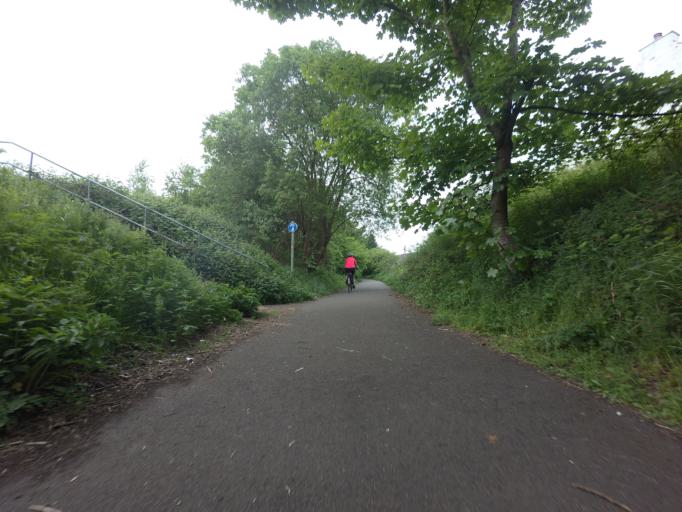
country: GB
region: Scotland
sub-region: Fife
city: Townhill
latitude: 56.0863
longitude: -3.4414
